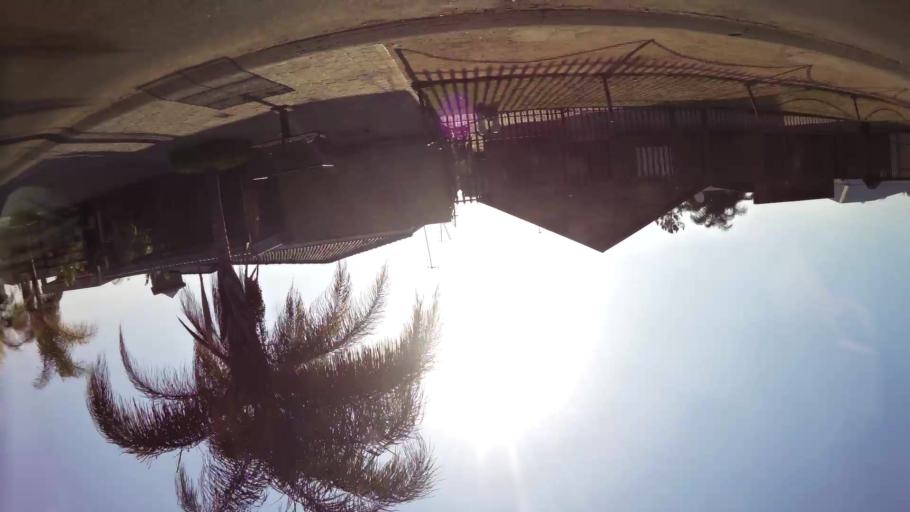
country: ZA
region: North-West
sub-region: Bojanala Platinum District Municipality
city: Rustenburg
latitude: -25.6453
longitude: 27.2395
